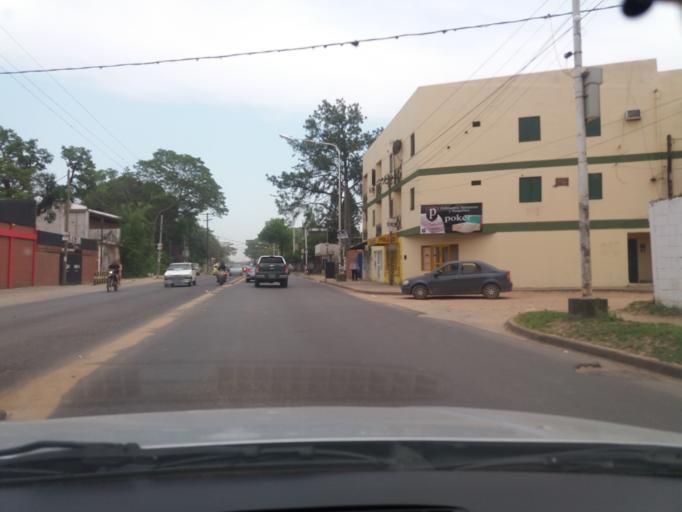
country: AR
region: Corrientes
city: Corrientes
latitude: -27.5034
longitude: -58.8122
